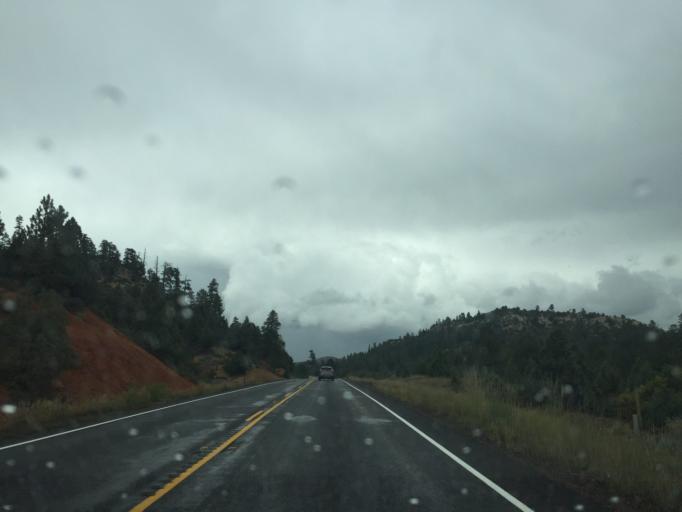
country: US
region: Utah
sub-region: Garfield County
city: Panguitch
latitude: 37.4497
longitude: -112.5323
